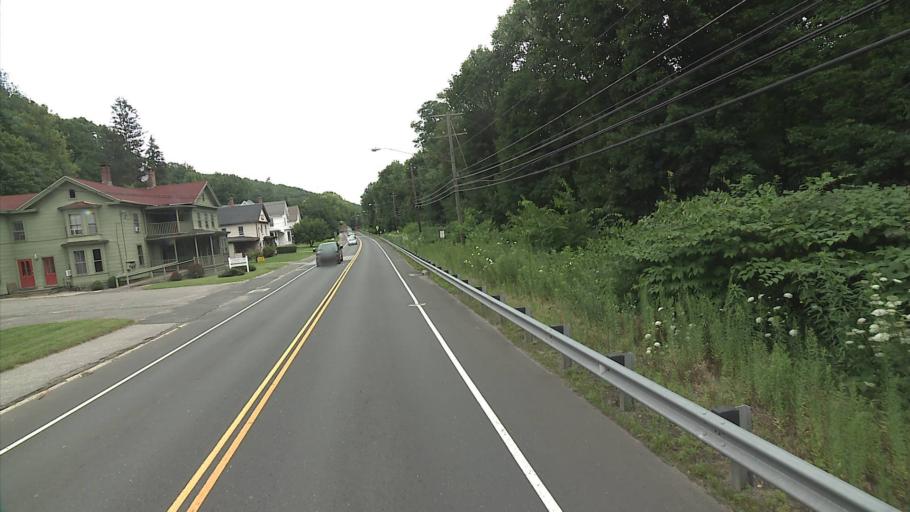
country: US
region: Connecticut
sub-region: Litchfield County
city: Winsted
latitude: 41.9266
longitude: -73.0596
